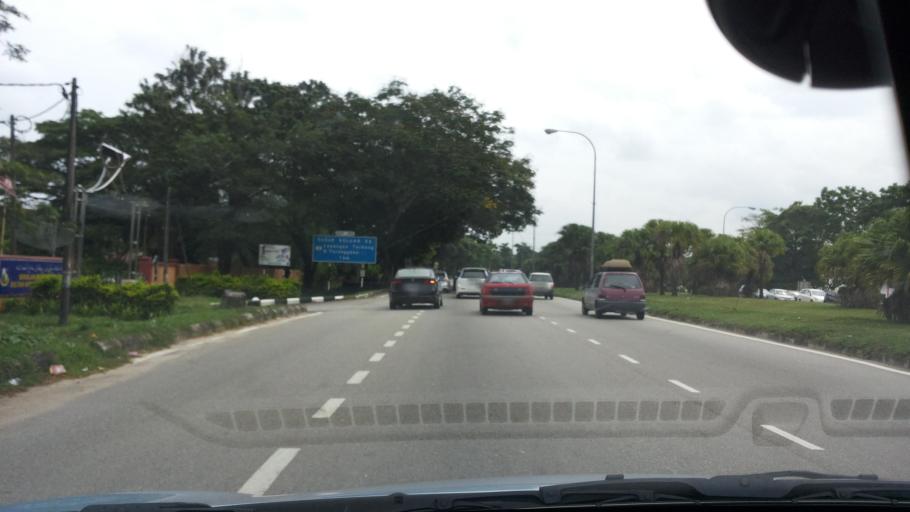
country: MY
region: Pahang
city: Kuantan
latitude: 3.7694
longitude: 103.2340
